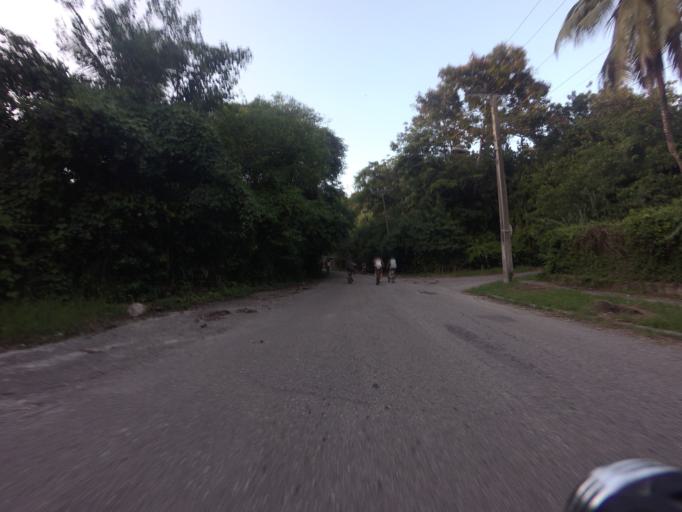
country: CU
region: La Habana
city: Cerro
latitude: 23.1113
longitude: -82.4051
